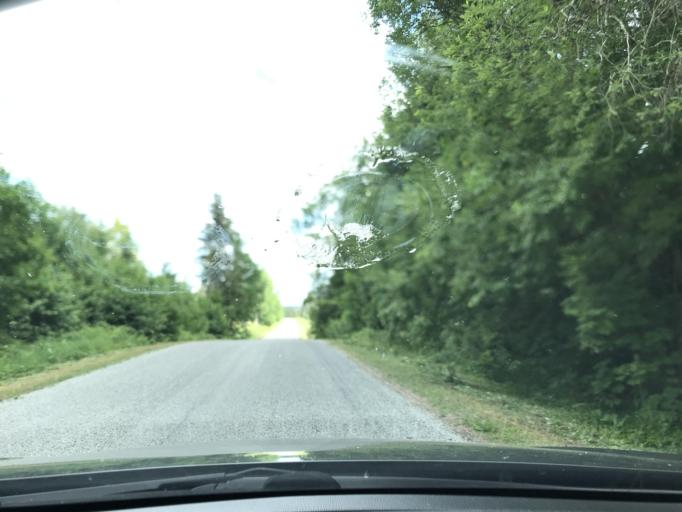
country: LV
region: Alsunga
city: Alsunga
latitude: 56.9927
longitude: 21.6250
